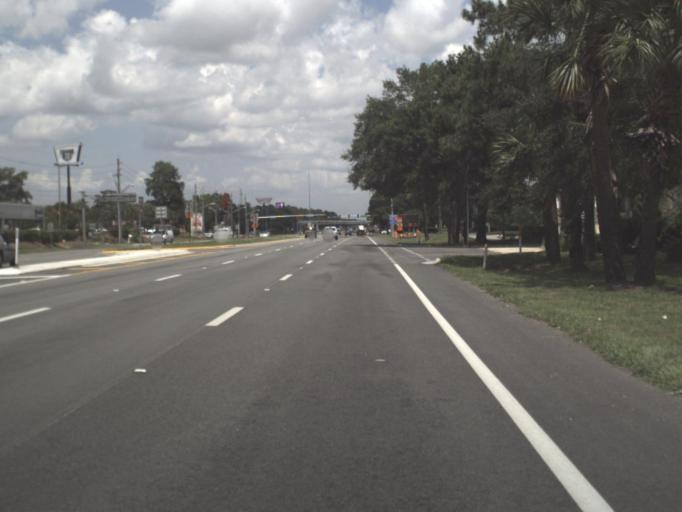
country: US
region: Florida
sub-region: Saint Johns County
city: Fruit Cove
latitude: 30.1797
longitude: -81.5528
